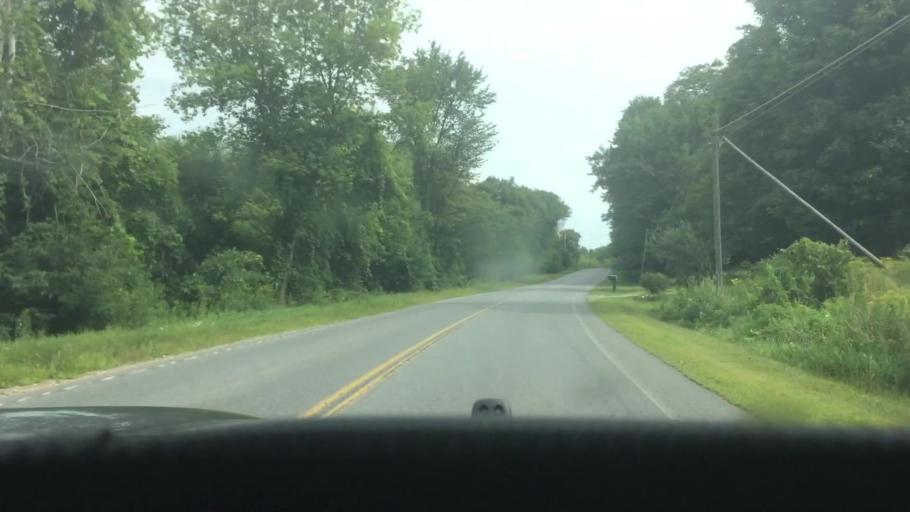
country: US
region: New York
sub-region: St. Lawrence County
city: Canton
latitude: 44.4760
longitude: -75.2269
